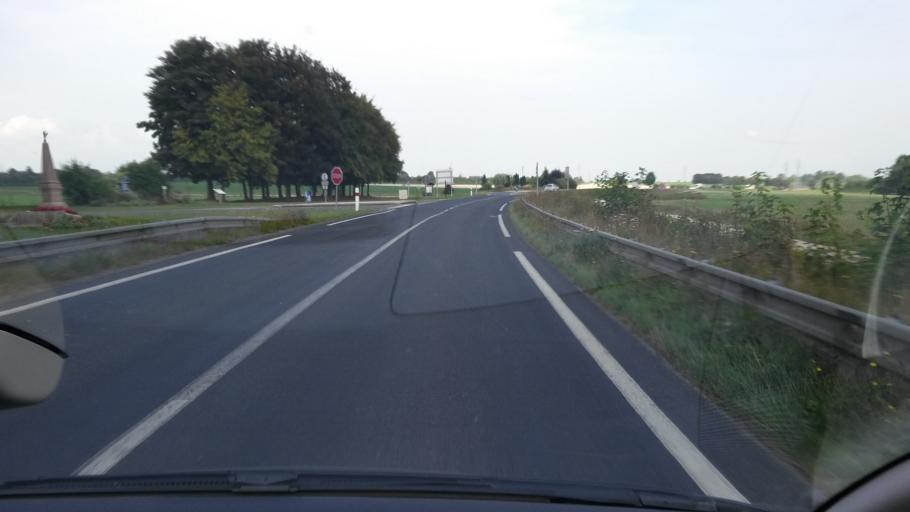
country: FR
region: Champagne-Ardenne
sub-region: Departement de la Marne
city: Fere-Champenoise
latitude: 48.7601
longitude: 3.9997
